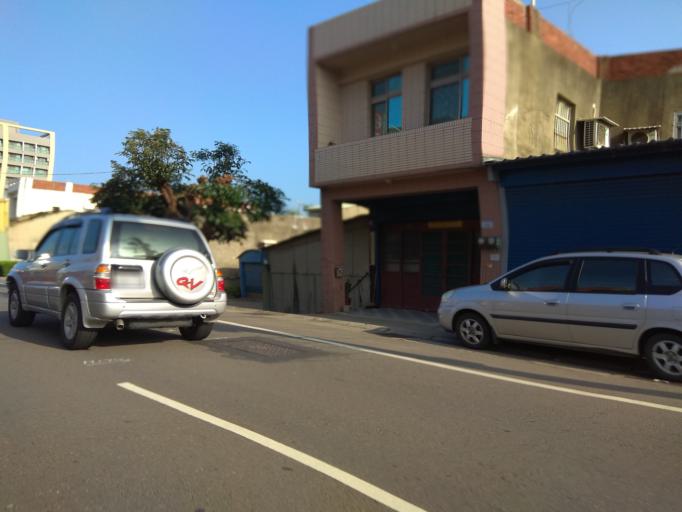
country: TW
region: Taiwan
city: Taoyuan City
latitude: 24.9636
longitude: 121.1432
